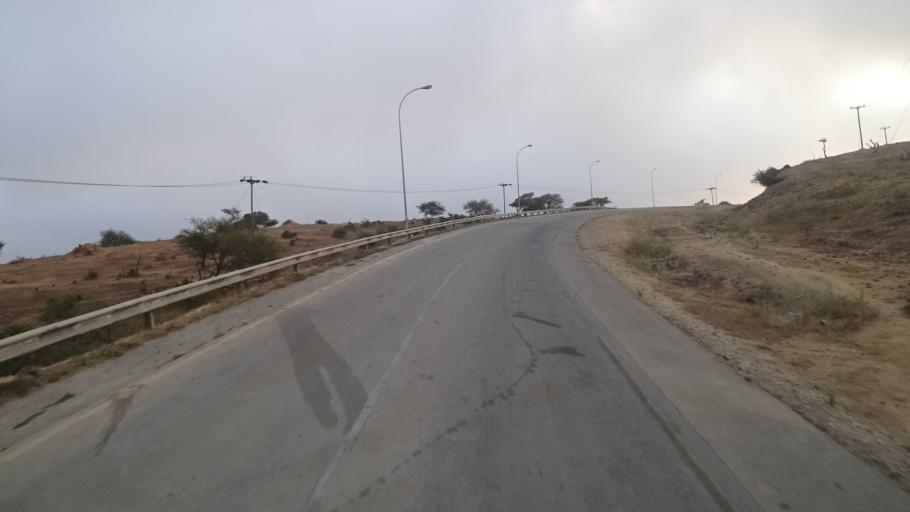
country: OM
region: Zufar
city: Salalah
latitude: 17.1374
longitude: 53.9668
